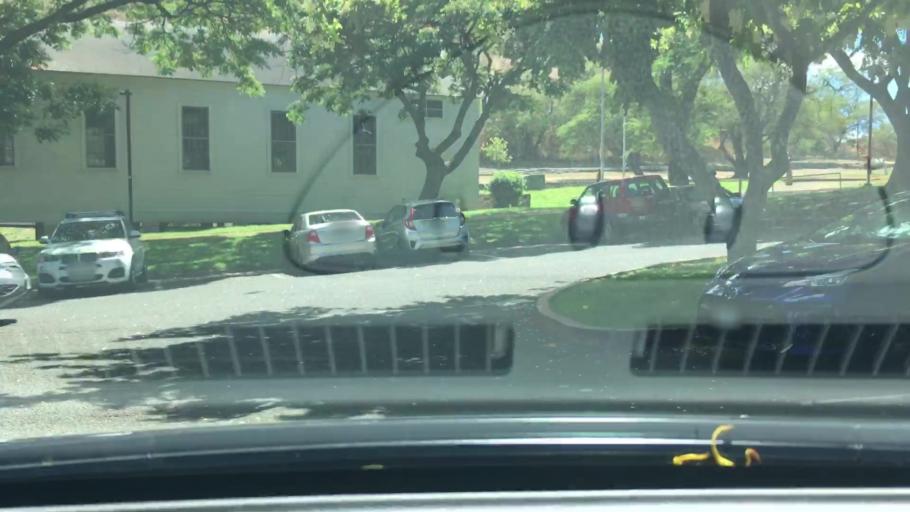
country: US
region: Hawaii
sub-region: Honolulu County
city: Honolulu
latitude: 21.2693
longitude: -157.8012
